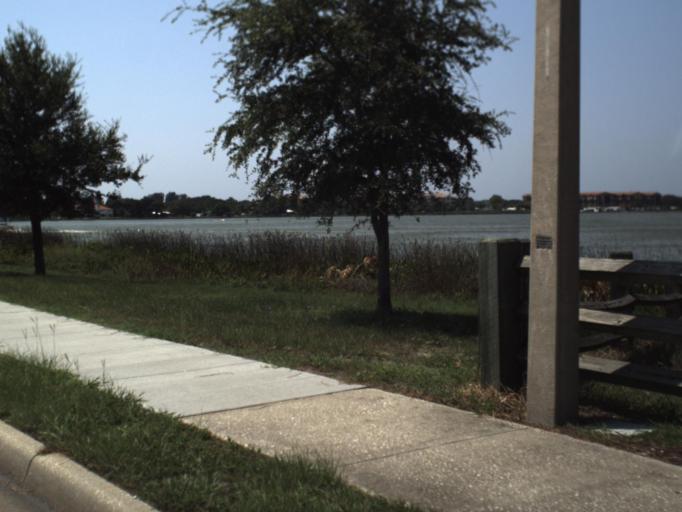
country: US
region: Florida
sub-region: Pinellas County
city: Seminole
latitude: 27.8395
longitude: -82.7775
